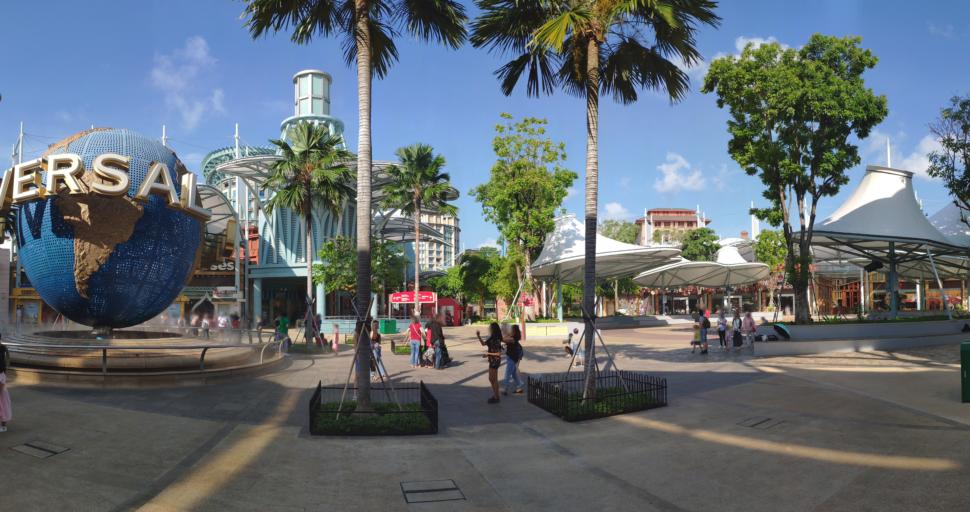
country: SG
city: Singapore
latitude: 1.2568
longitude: 103.8213
